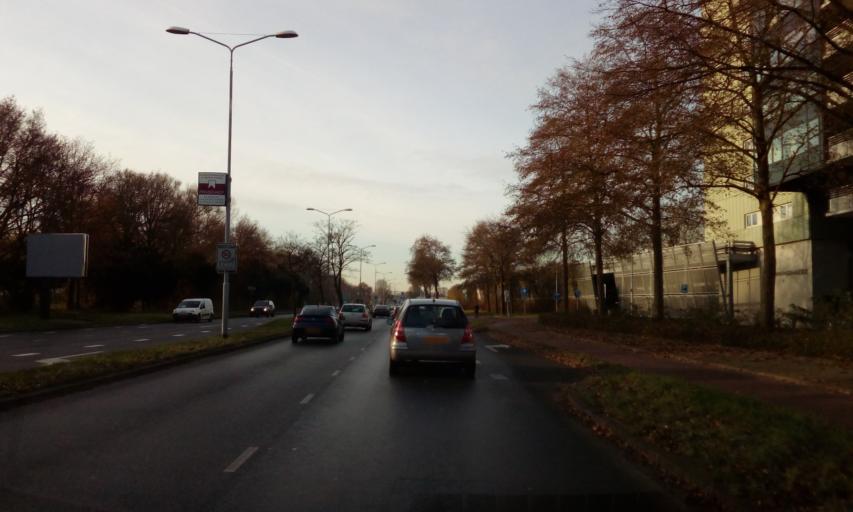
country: NL
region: South Holland
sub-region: Gemeente Leidschendam-Voorburg
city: Voorburg
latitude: 52.0883
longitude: 4.3875
